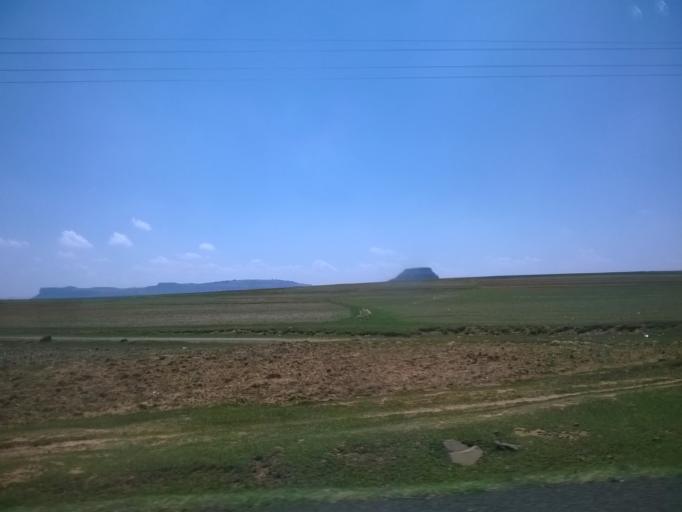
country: LS
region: Leribe
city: Leribe
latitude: -28.9757
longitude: 27.9824
